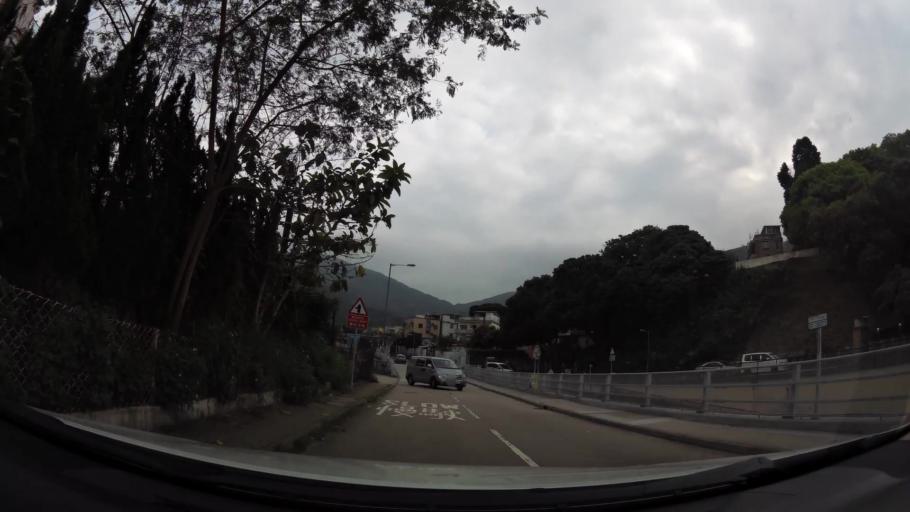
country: HK
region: Tai Po
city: Tai Po
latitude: 22.4374
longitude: 114.1647
